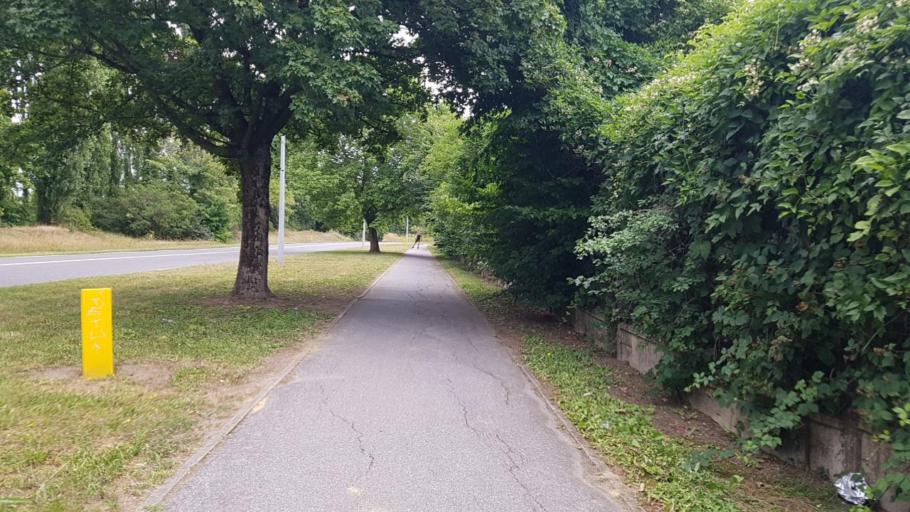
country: FR
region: Picardie
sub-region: Departement de l'Oise
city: Clairoix
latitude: 49.4327
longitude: 2.8551
